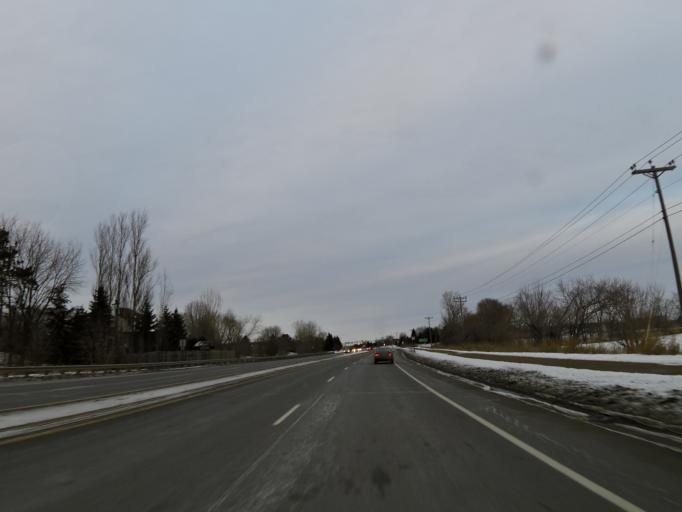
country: US
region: Minnesota
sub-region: Washington County
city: Woodbury
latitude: 44.9345
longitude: -92.9042
